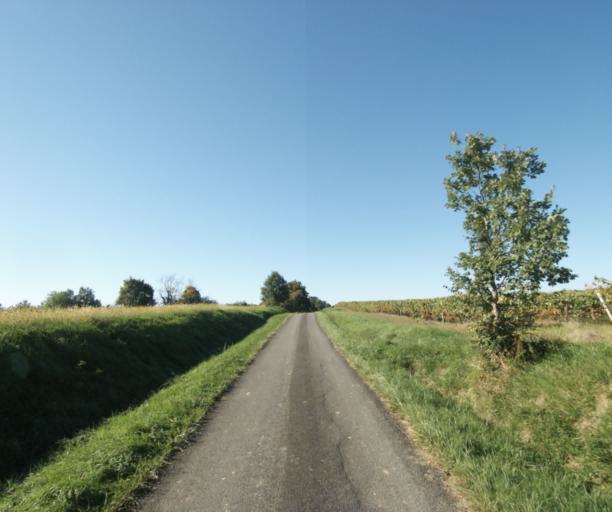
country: FR
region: Midi-Pyrenees
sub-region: Departement du Gers
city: Gondrin
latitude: 43.8133
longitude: 0.2048
